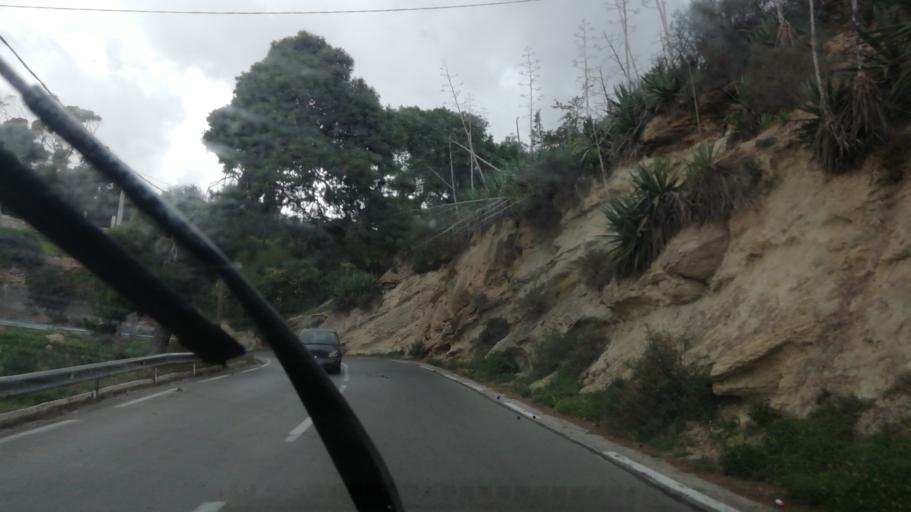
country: DZ
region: Oran
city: Oran
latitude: 35.7027
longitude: -0.6610
